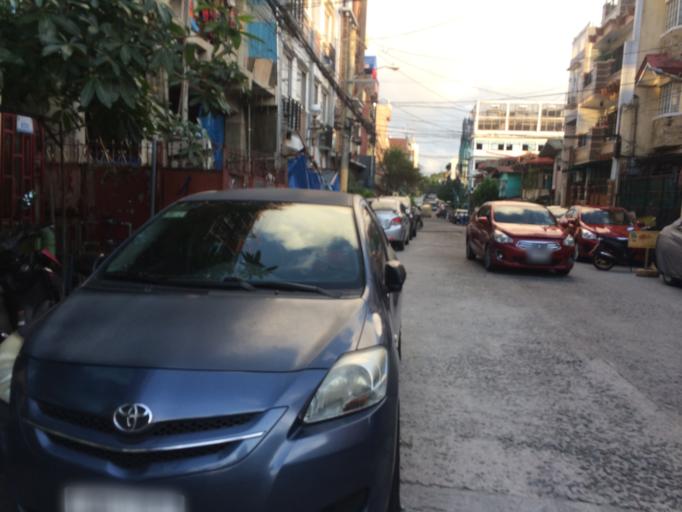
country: PH
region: Metro Manila
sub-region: City of Manila
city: Manila
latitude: 14.6105
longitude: 121.0084
